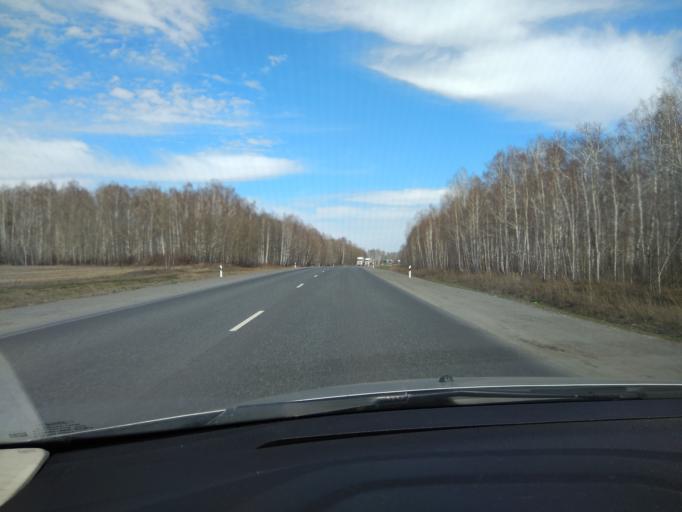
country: RU
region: Sverdlovsk
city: Pyshma
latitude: 56.9277
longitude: 63.1542
